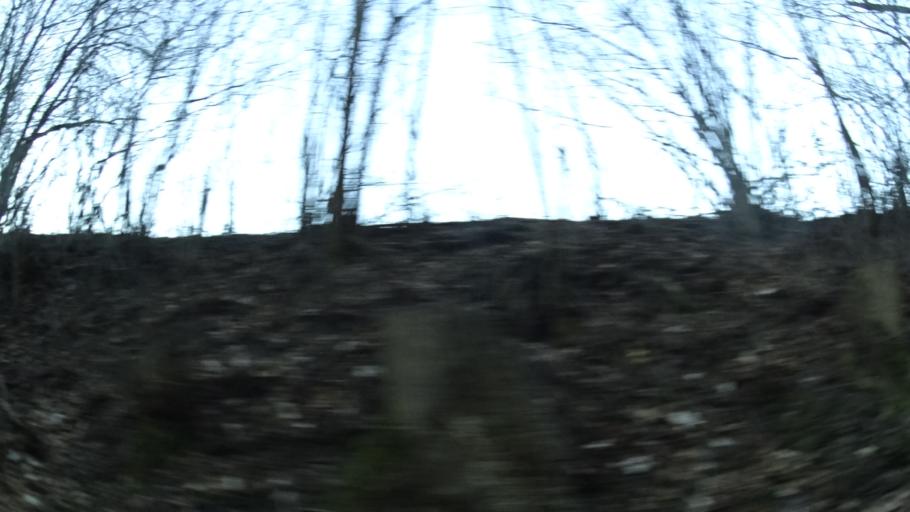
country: DE
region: Thuringia
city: Grafenthal
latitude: 50.5326
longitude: 11.3024
